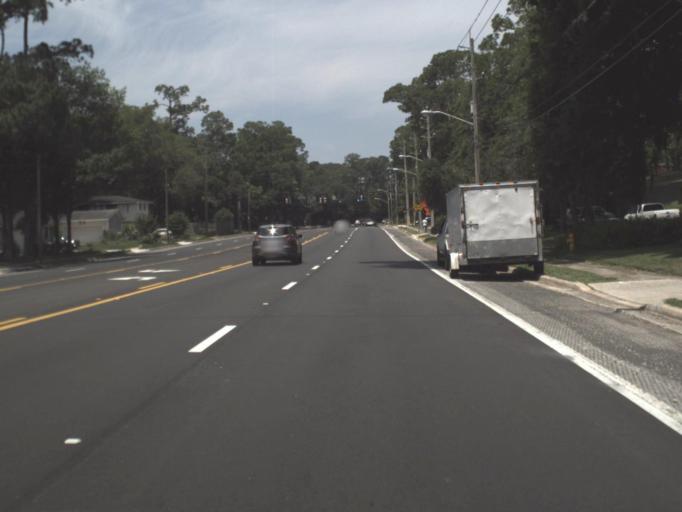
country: US
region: Florida
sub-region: Duval County
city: Jacksonville
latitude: 30.2475
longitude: -81.6333
